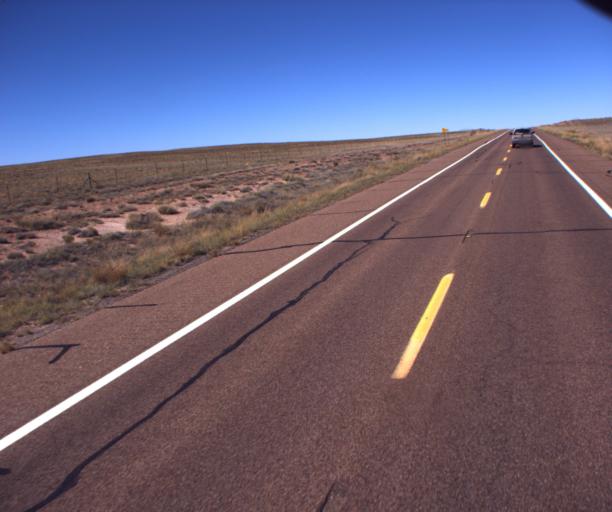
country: US
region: Arizona
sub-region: Navajo County
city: Holbrook
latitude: 34.8084
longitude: -109.9156
